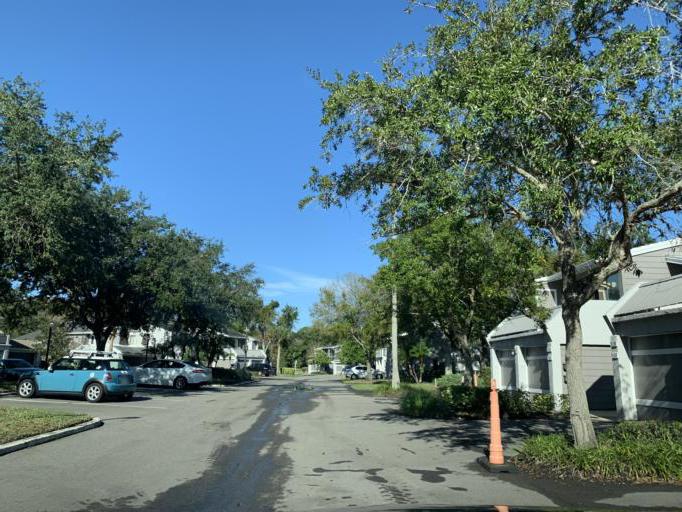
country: US
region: Florida
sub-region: Orange County
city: Oak Ridge
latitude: 28.4871
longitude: -81.4490
